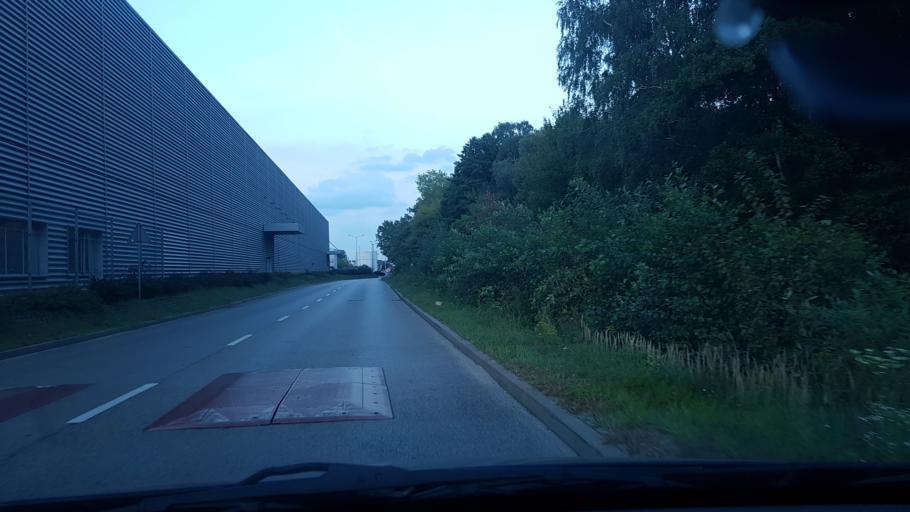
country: PL
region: Masovian Voivodeship
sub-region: Powiat wolominski
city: Zabki
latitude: 52.3021
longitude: 21.0787
